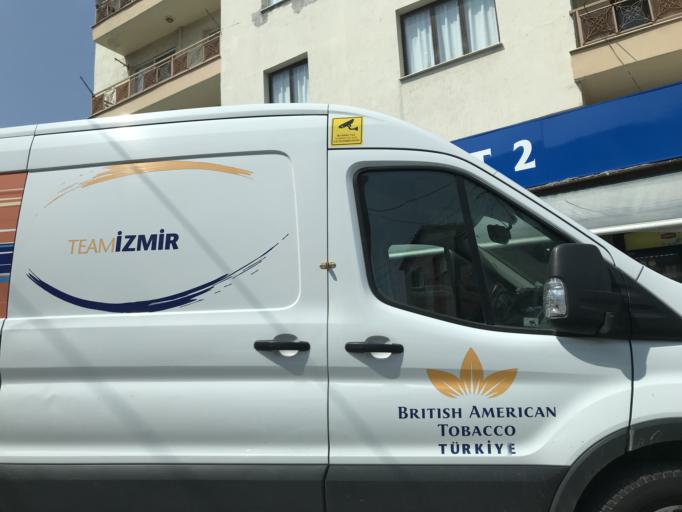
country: TR
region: Izmir
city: Karabaglar
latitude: 38.3877
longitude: 27.1307
